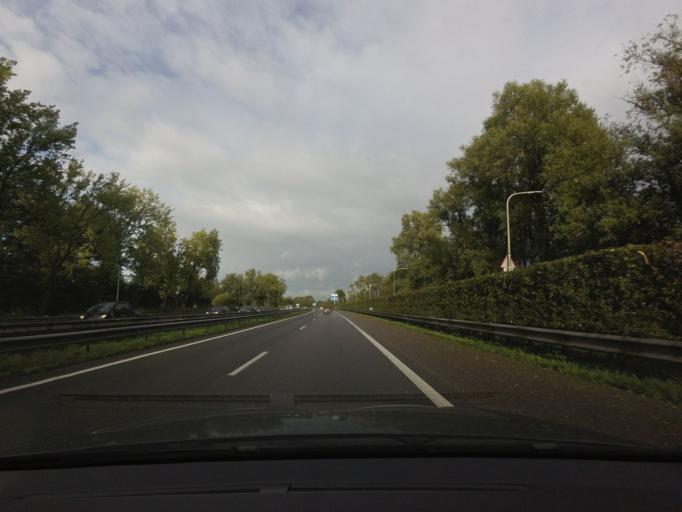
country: NL
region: South Holland
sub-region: Gemeente Voorschoten
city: Voorschoten
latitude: 52.1509
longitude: 4.4354
